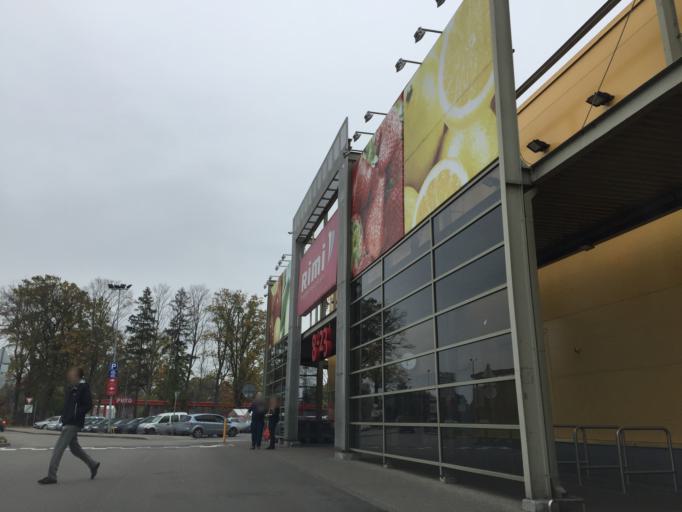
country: LV
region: Marupe
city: Marupe
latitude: 56.9296
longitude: 24.0379
